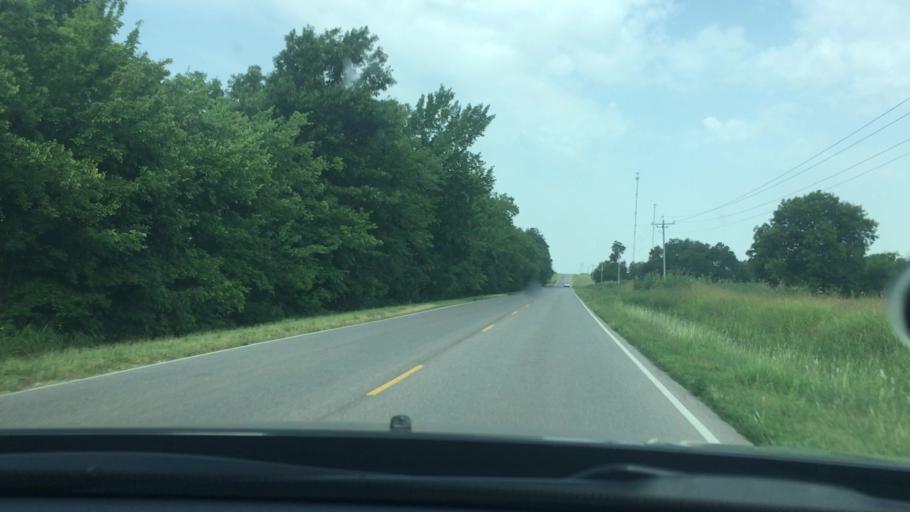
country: US
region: Oklahoma
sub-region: Garvin County
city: Stratford
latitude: 34.7967
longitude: -96.8721
